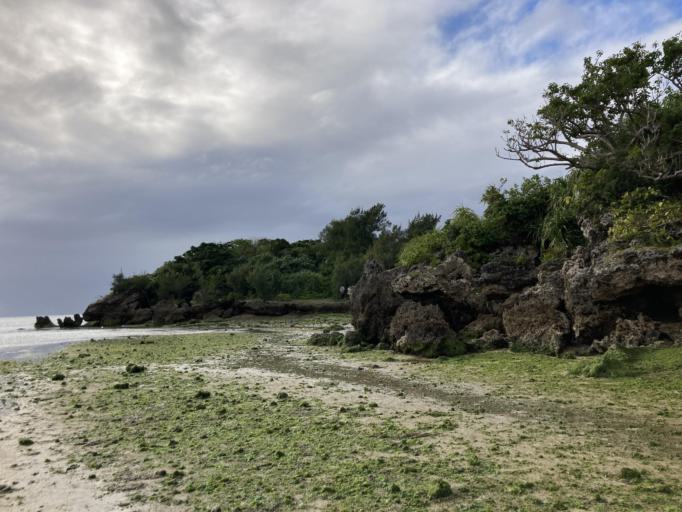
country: JP
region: Okinawa
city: Itoman
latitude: 26.1085
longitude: 127.6608
